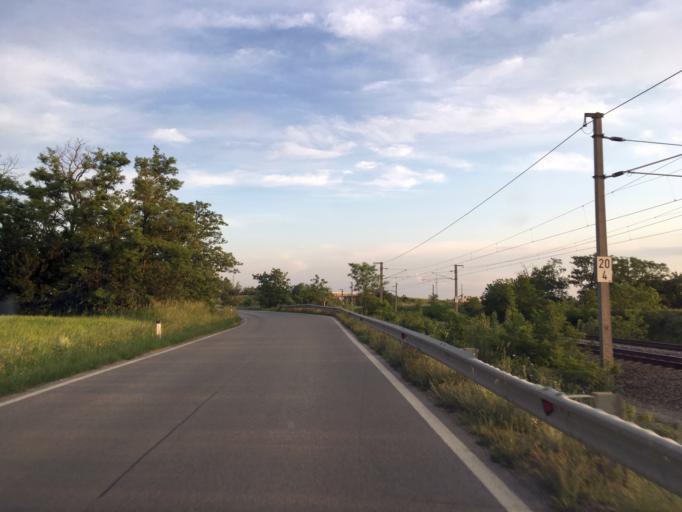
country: AT
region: Lower Austria
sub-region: Politischer Bezirk Wien-Umgebung
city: Gerasdorf bei Wien
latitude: 48.3084
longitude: 16.4912
